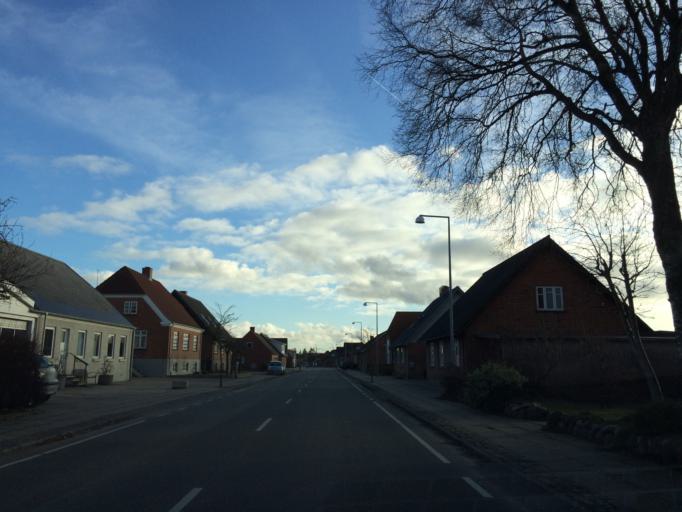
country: DK
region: Central Jutland
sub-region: Lemvig Kommune
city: Lemvig
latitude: 56.4155
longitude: 8.3078
